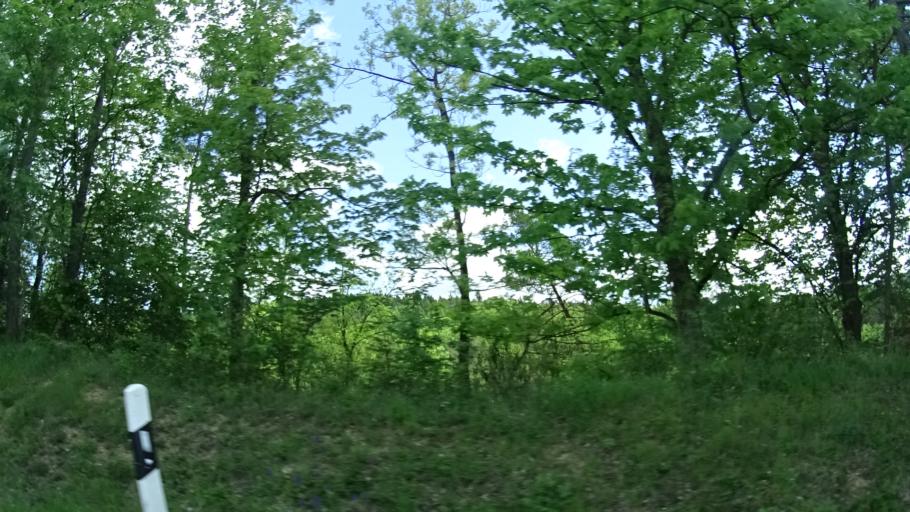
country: DE
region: Thuringia
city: Leutersdorf
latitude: 50.5313
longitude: 10.5486
